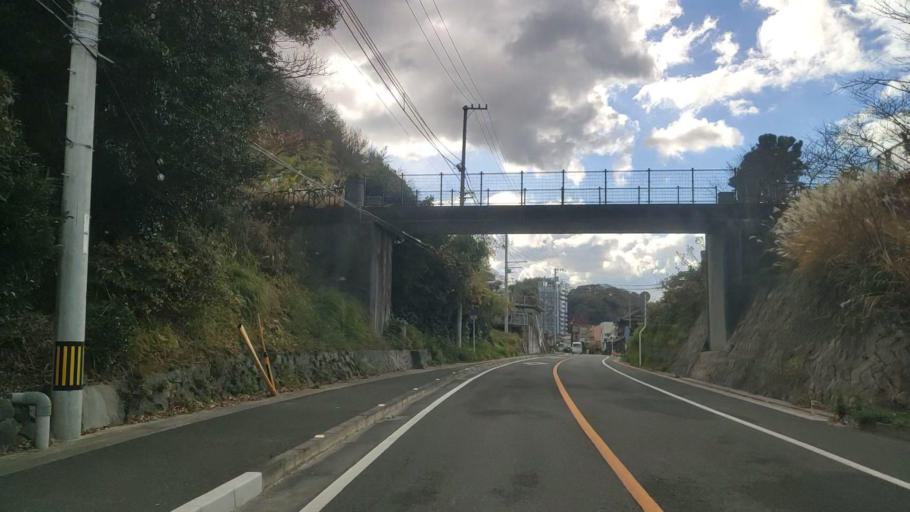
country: JP
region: Ehime
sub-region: Shikoku-chuo Shi
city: Matsuyama
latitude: 33.8737
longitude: 132.7090
